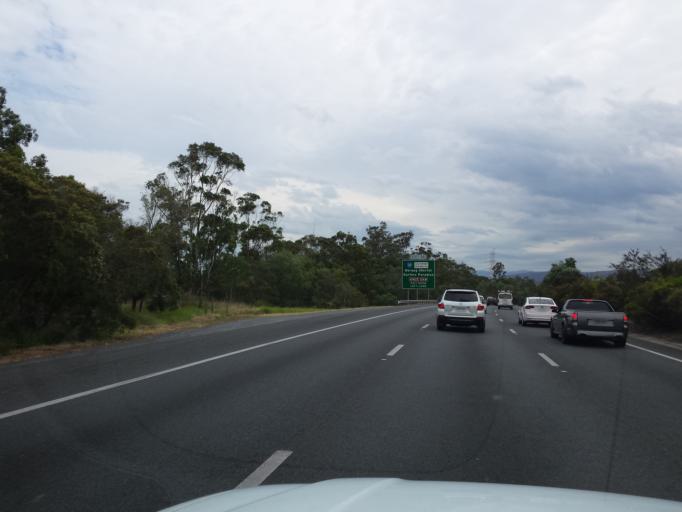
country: AU
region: Queensland
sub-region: Gold Coast
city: Nerang
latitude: -27.9720
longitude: 153.3470
